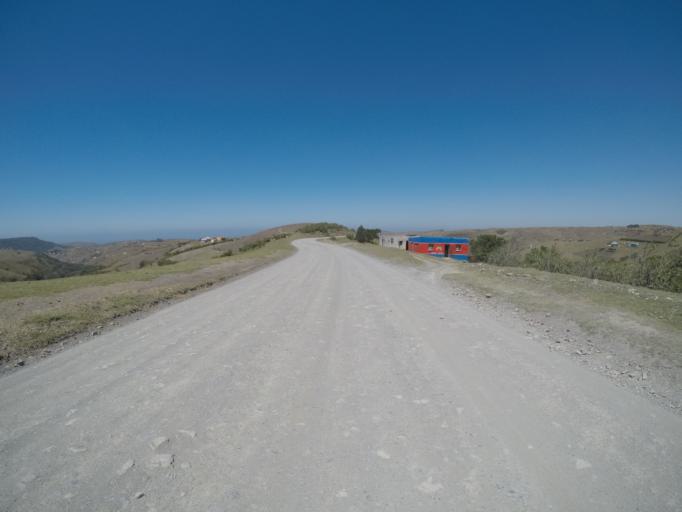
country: ZA
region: Eastern Cape
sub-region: OR Tambo District Municipality
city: Libode
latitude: -31.9891
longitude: 29.0535
